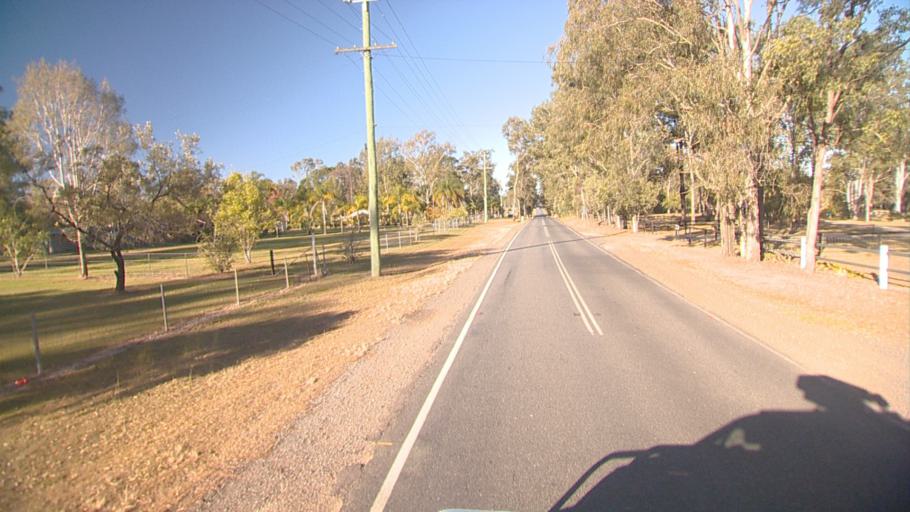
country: AU
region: Queensland
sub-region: Logan
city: North Maclean
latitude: -27.7577
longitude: 153.0298
